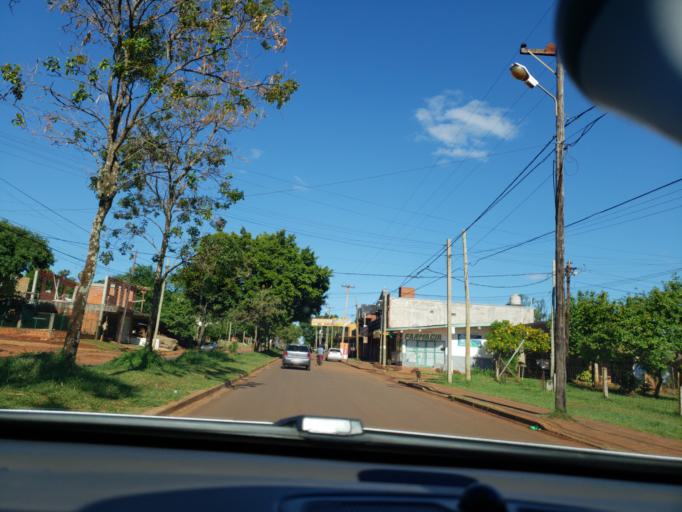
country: AR
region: Misiones
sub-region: Departamento de Capital
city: Posadas
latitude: -27.3832
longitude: -55.9409
